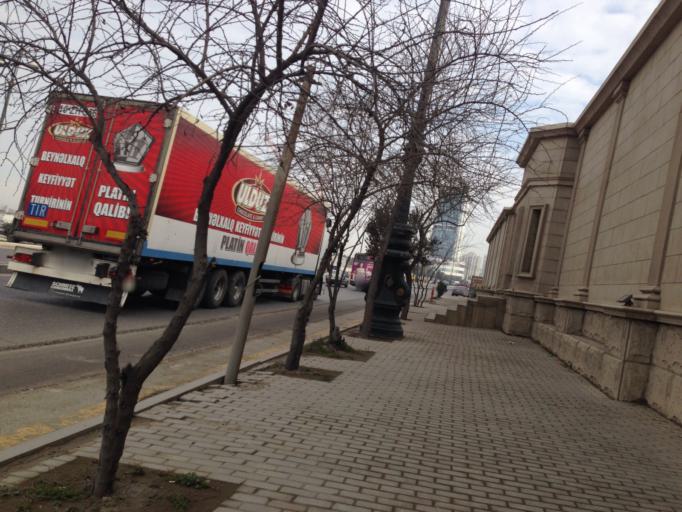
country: AZ
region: Baki
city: Baku
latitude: 40.4107
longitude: 49.8958
